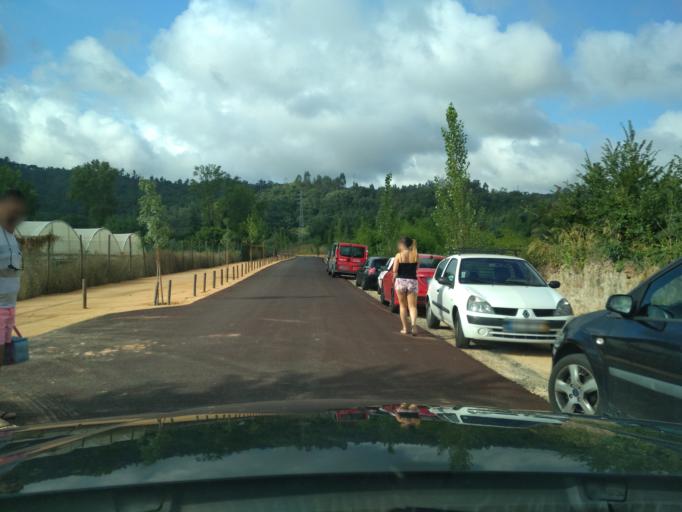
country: PT
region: Coimbra
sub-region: Coimbra
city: Coimbra
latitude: 40.1827
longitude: -8.4155
